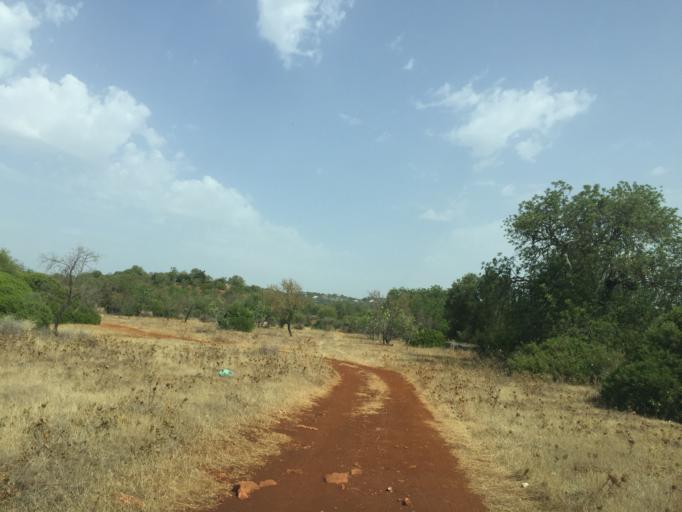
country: PT
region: Faro
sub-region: Loule
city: Boliqueime
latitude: 37.1319
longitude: -8.1348
